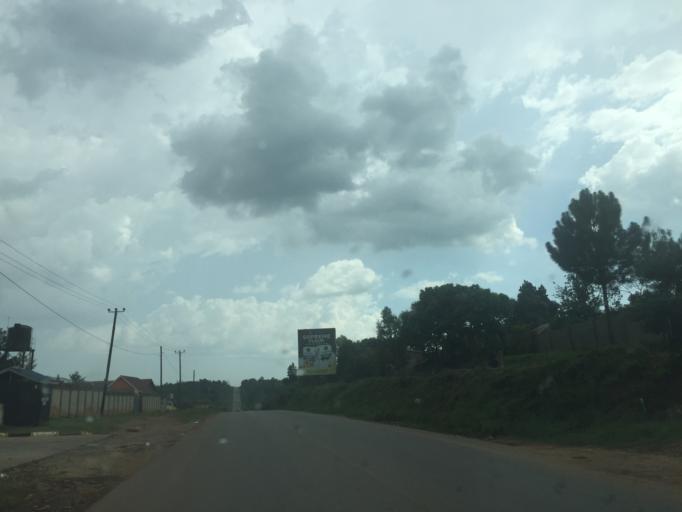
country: UG
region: Central Region
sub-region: Luwero District
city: Wobulenzi
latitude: 0.6068
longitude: 32.5322
